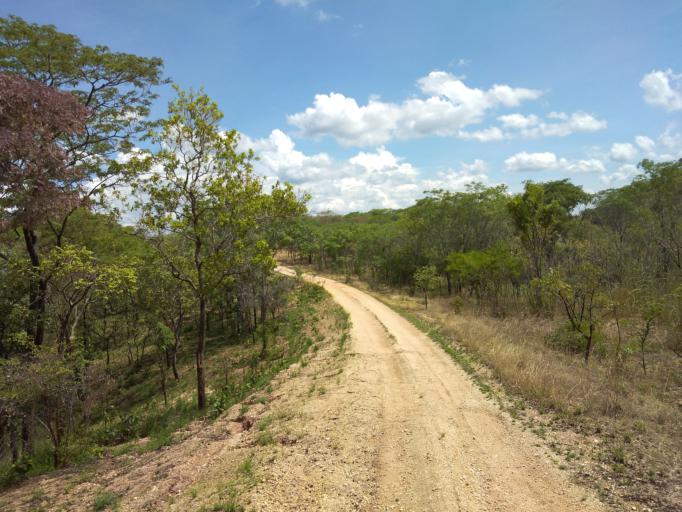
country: ZM
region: Central
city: Mkushi
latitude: -14.1207
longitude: 30.0120
